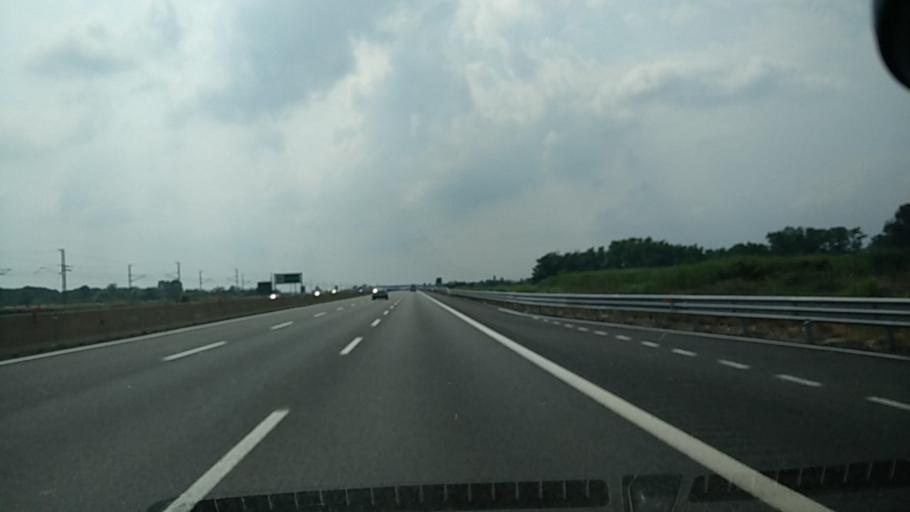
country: IT
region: Piedmont
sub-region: Provincia di Novara
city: San Pietro Mosezzo
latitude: 45.4728
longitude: 8.5475
